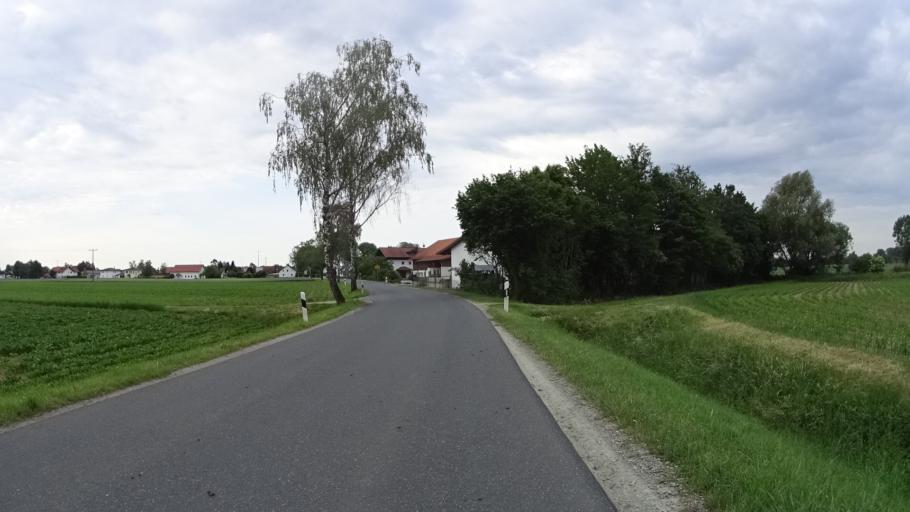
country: DE
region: Bavaria
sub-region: Lower Bavaria
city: Parkstetten
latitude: 48.9136
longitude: 12.6232
